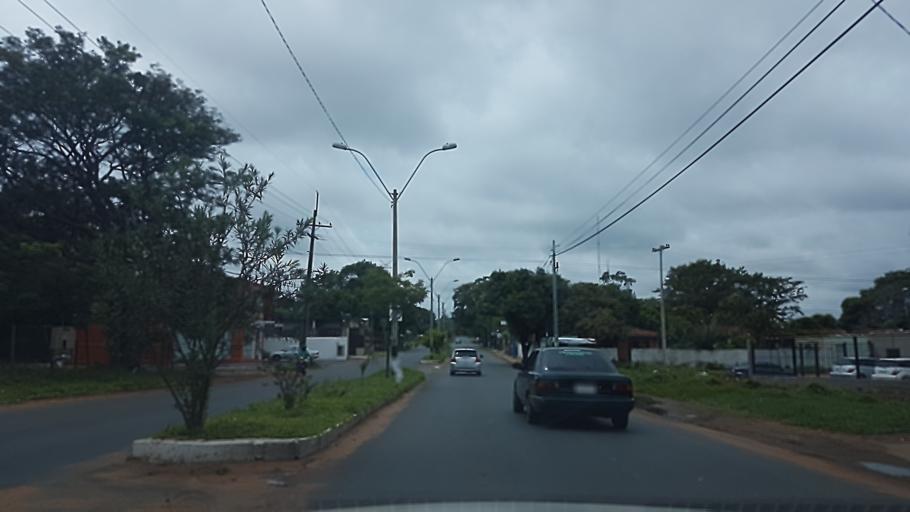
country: PY
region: Central
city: Villa Elisa
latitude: -25.3913
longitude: -57.5825
